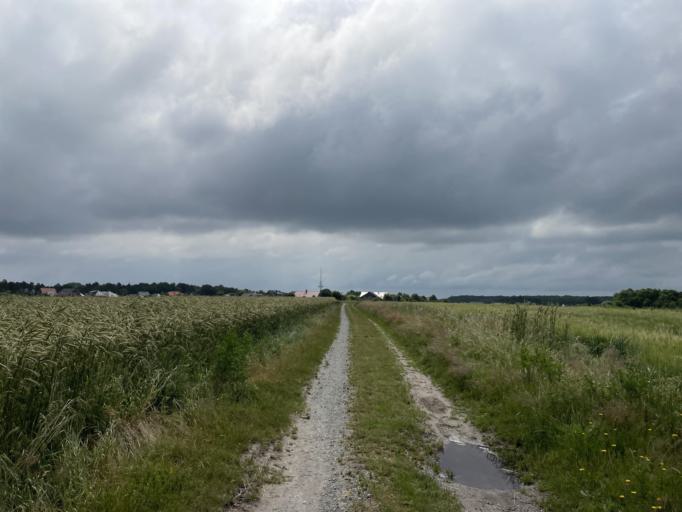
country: DE
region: Lower Saxony
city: Cuxhaven
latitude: 53.8777
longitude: 8.6454
